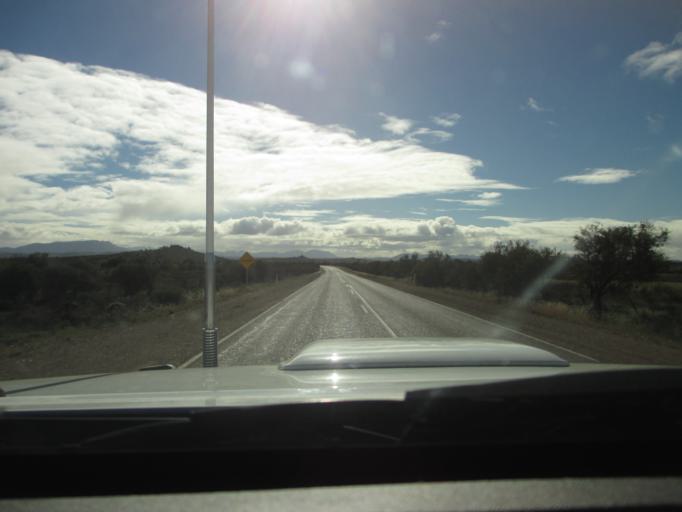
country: AU
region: South Australia
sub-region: Flinders Ranges
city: Quorn
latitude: -31.9079
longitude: 138.4341
